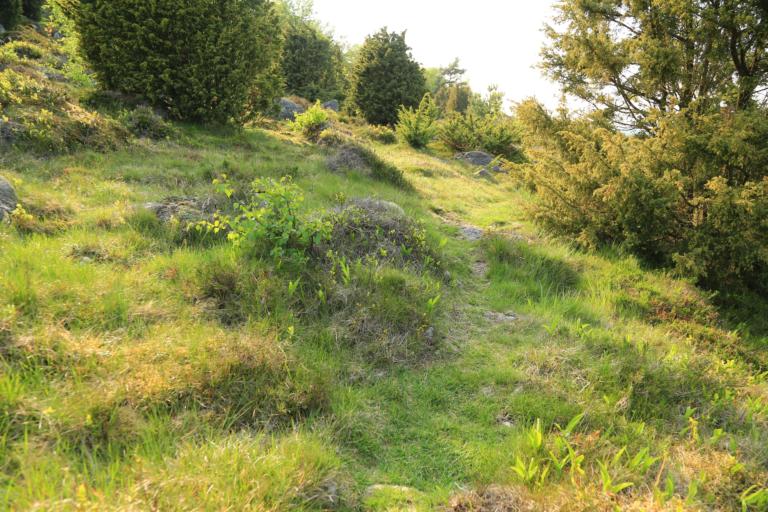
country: SE
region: Halland
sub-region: Varbergs Kommun
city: Varberg
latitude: 57.1609
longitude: 12.2395
